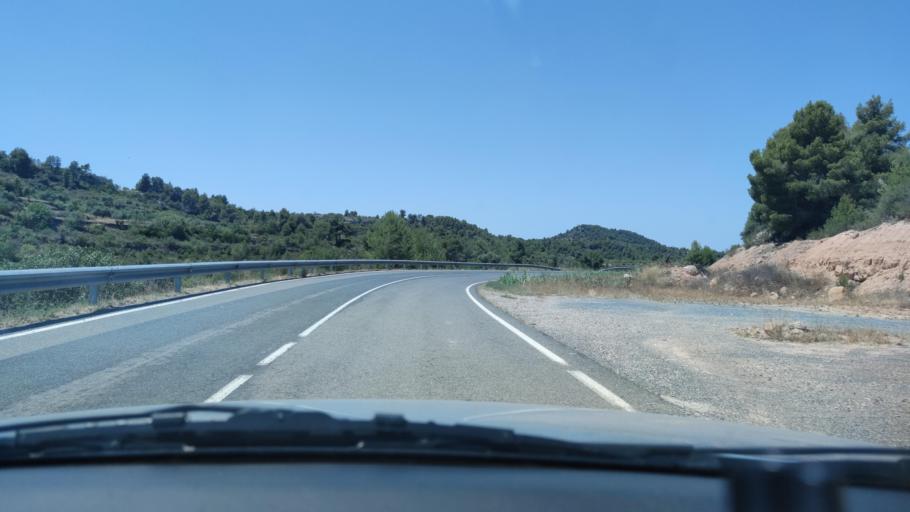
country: ES
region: Catalonia
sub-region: Provincia de Lleida
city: Juncosa
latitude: 41.3789
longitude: 0.7526
